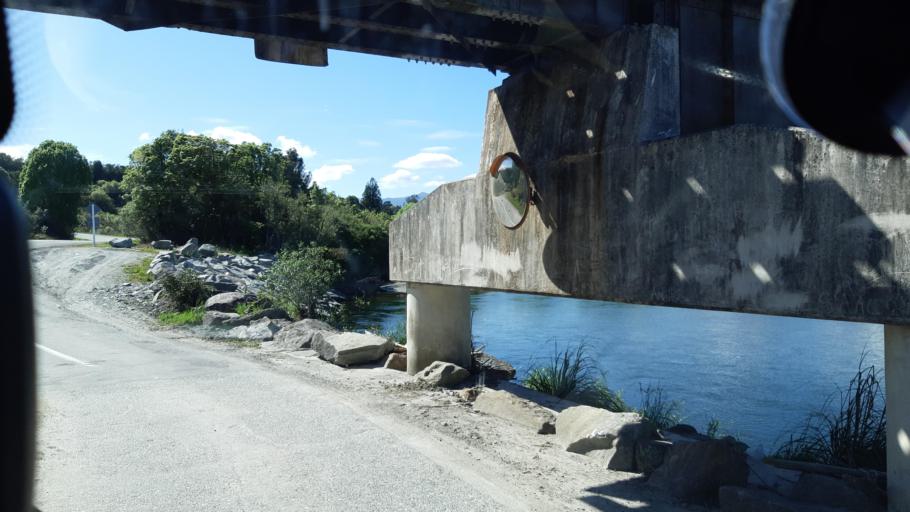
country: NZ
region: West Coast
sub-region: Grey District
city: Greymouth
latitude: -42.6014
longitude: 171.5063
